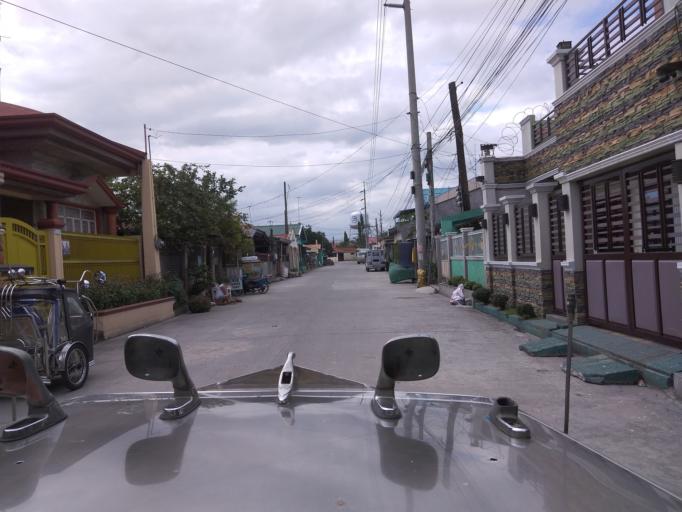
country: PH
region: Central Luzon
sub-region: Province of Pampanga
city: Pandacaqui
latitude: 15.1795
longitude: 120.6499
